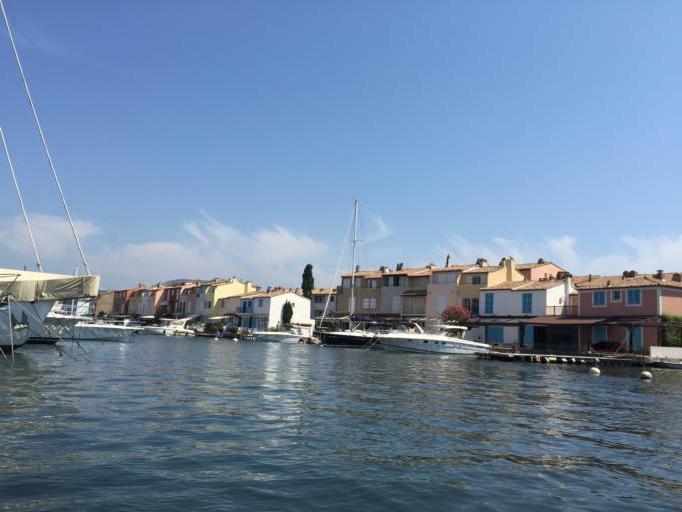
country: FR
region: Provence-Alpes-Cote d'Azur
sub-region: Departement du Var
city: Gassin
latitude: 43.2729
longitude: 6.5830
